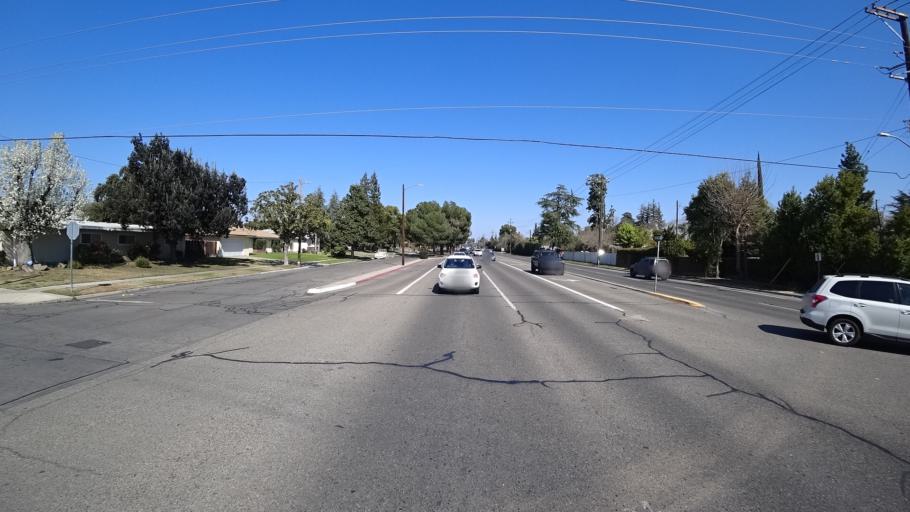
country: US
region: California
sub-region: Fresno County
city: Fresno
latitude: 36.8028
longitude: -119.8265
